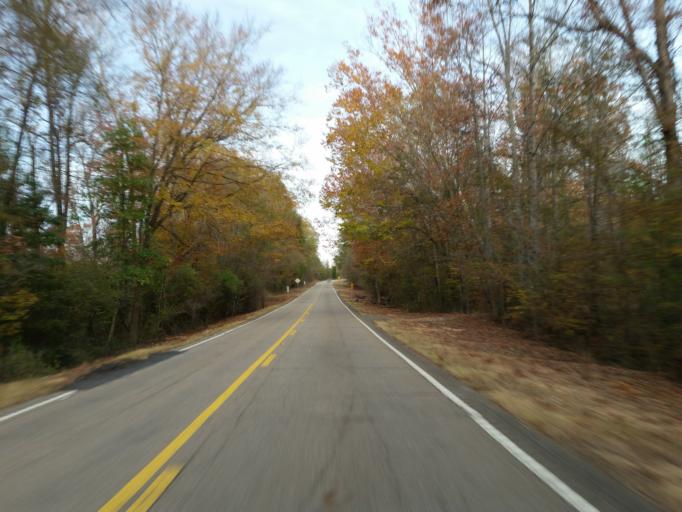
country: US
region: Alabama
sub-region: Sumter County
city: York
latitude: 32.4256
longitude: -88.4667
